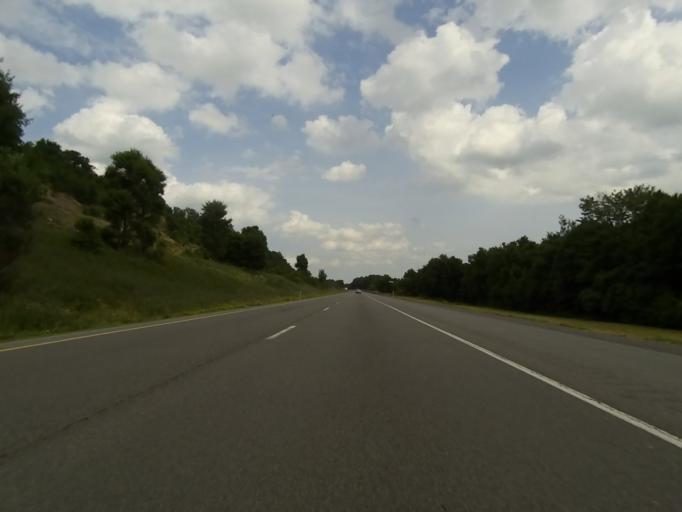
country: US
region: Pennsylvania
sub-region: Clearfield County
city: Clearfield
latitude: 41.0723
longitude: -78.4893
